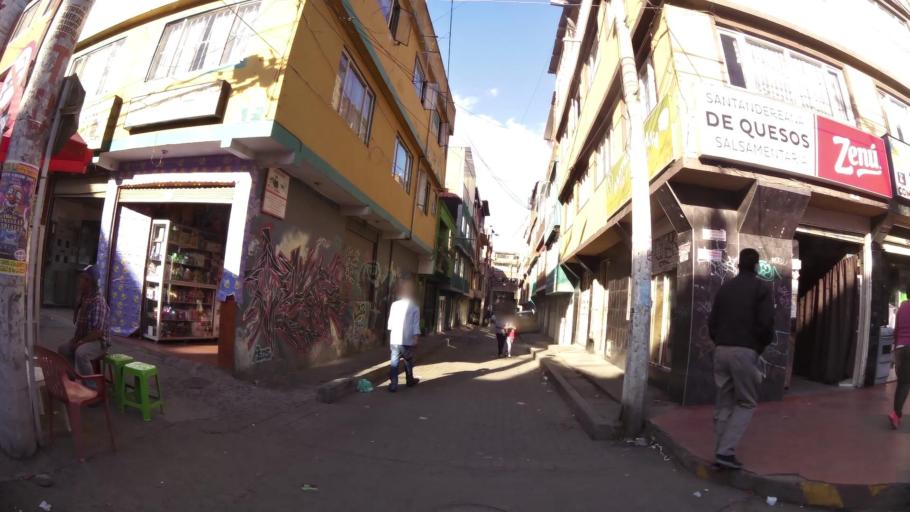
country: CO
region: Cundinamarca
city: Soacha
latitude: 4.5762
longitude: -74.1535
